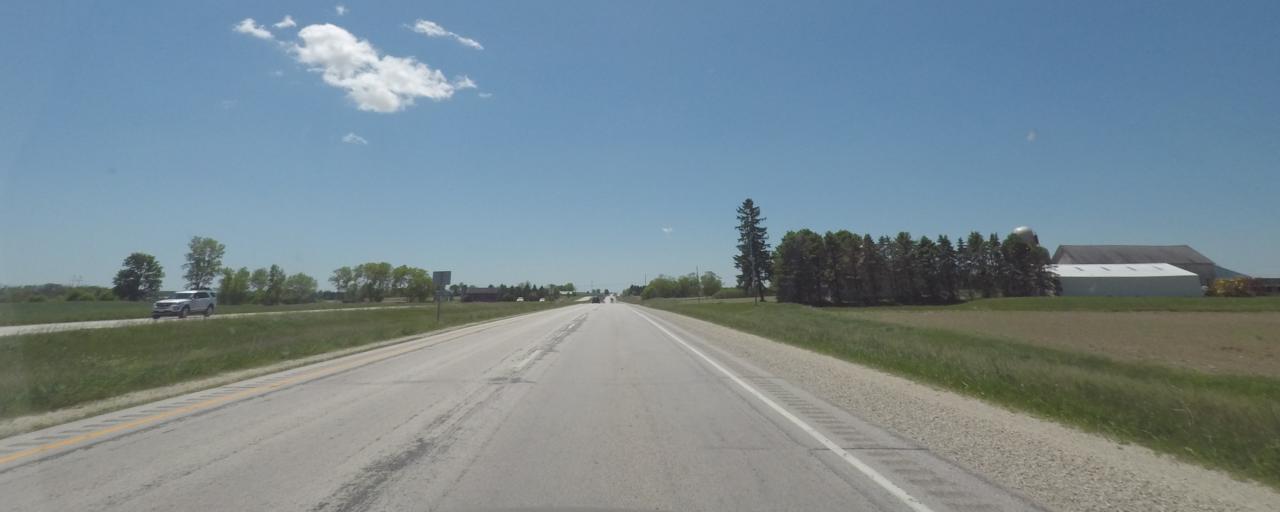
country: US
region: Wisconsin
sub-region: Sheboygan County
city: Plymouth
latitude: 43.7165
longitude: -87.9410
